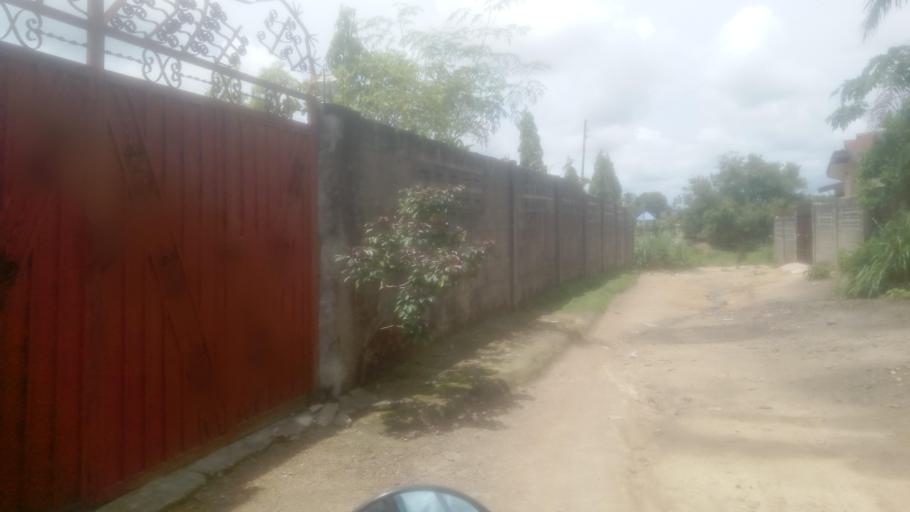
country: SL
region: Southern Province
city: Bo
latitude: 7.9526
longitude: -11.7123
